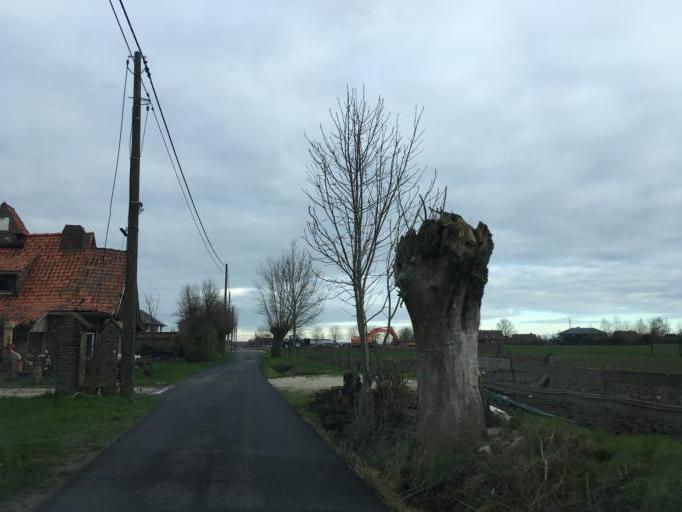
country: BE
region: Flanders
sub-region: Provincie West-Vlaanderen
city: Ledegem
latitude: 50.8988
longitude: 3.1380
